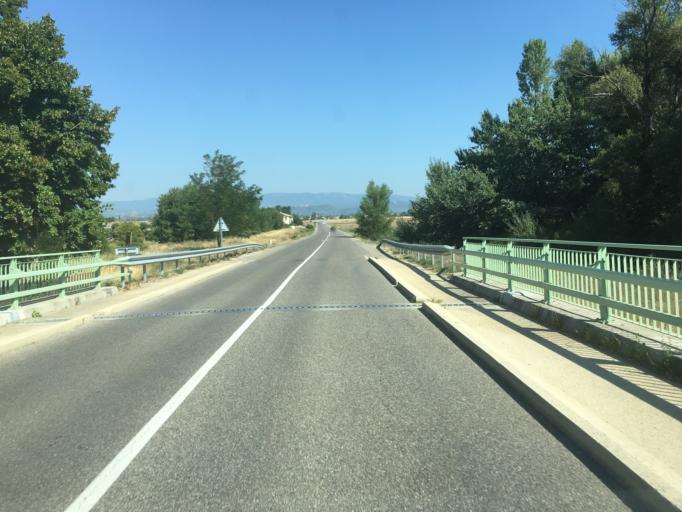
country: FR
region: Provence-Alpes-Cote d'Azur
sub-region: Departement des Alpes-de-Haute-Provence
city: Oraison
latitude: 43.8795
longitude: 5.9095
